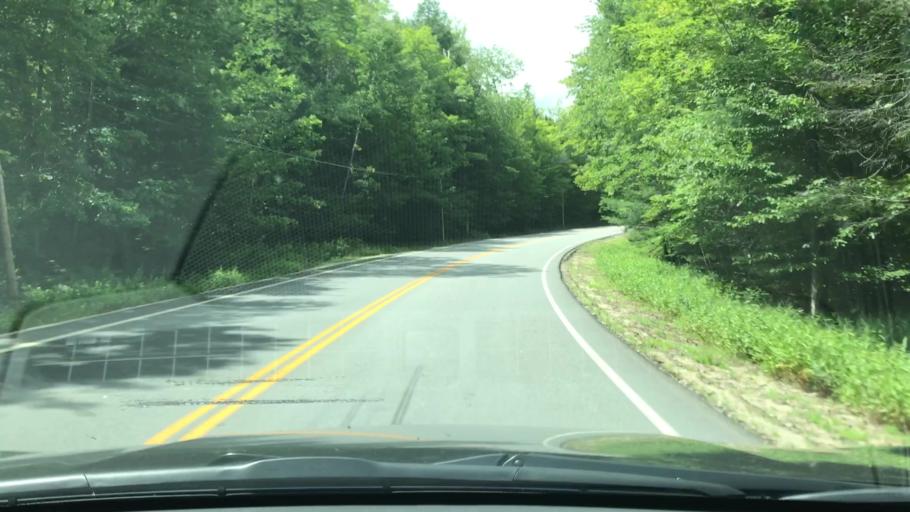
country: US
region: Maine
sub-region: Oxford County
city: Hartford
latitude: 44.3766
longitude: -70.4117
